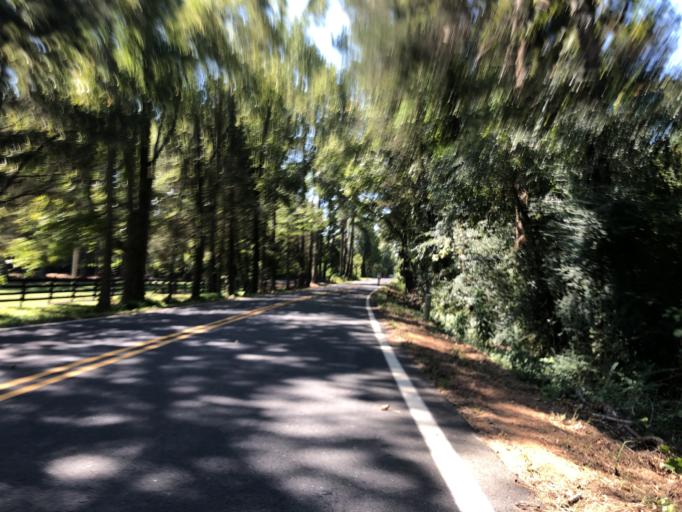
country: US
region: Georgia
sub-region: Heard County
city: Franklin
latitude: 33.3837
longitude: -84.9685
